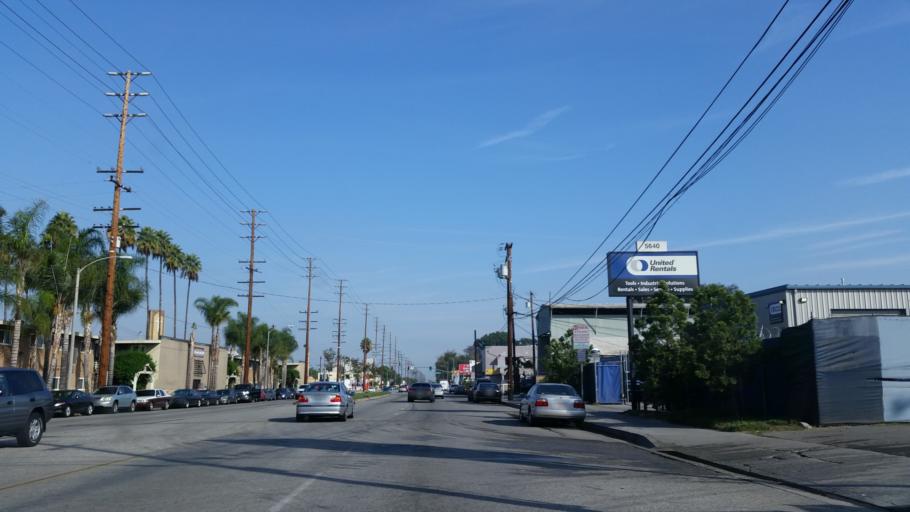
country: US
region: California
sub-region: Los Angeles County
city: Paramount
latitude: 33.8582
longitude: -118.1685
